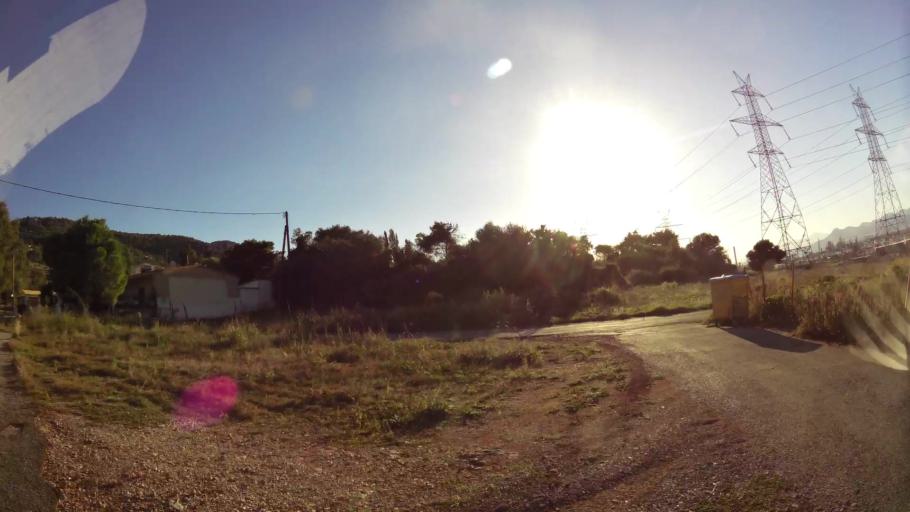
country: GR
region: Attica
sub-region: Nomarchia Athinas
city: Skaramangas
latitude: 38.0350
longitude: 23.6282
